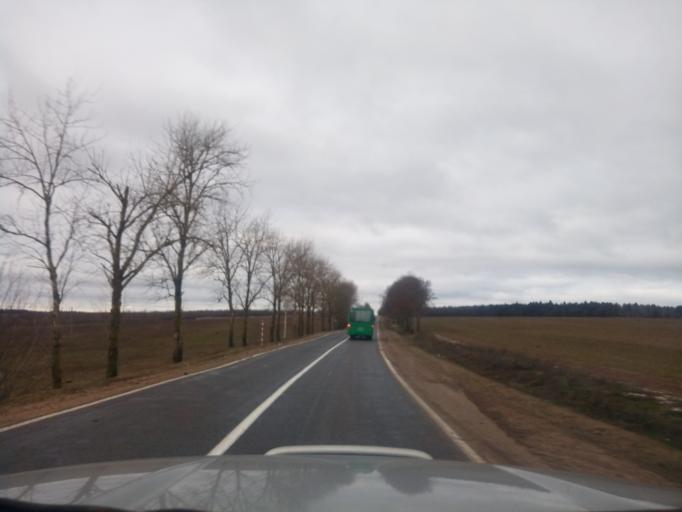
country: BY
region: Minsk
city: Kapyl'
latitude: 53.1719
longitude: 27.1585
